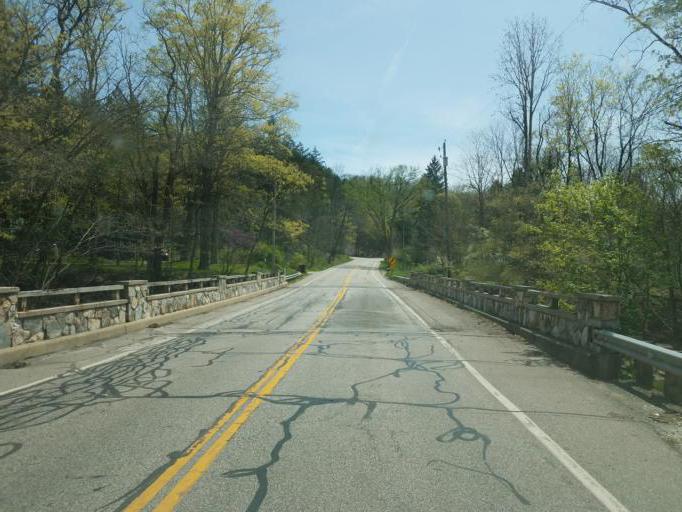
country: US
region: Ohio
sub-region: Summit County
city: Peninsula
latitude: 41.2077
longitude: -81.5845
